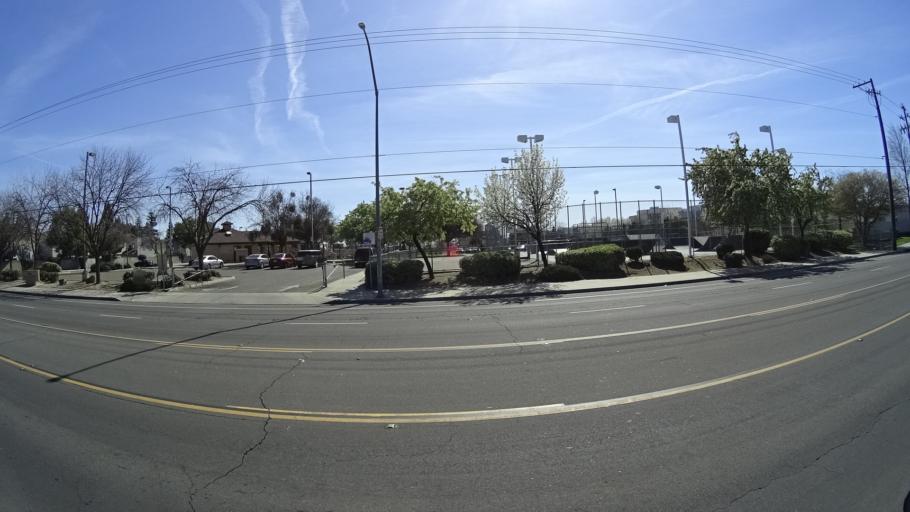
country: US
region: California
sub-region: Fresno County
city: Clovis
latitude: 36.8447
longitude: -119.7787
